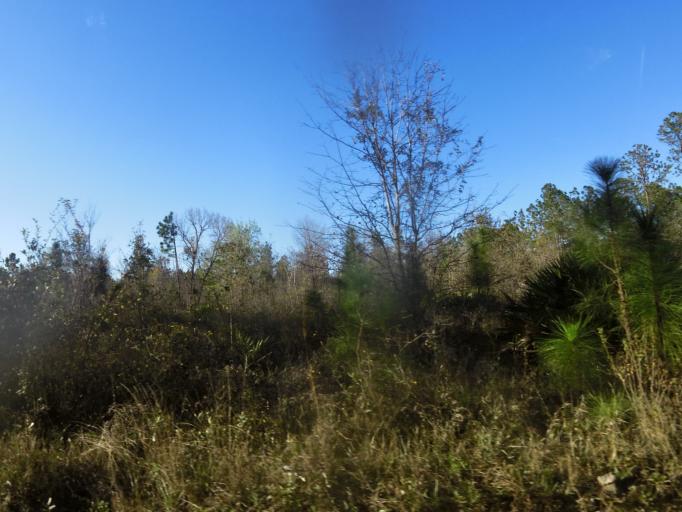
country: US
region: Florida
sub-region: Clay County
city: Middleburg
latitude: 30.1495
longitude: -81.8922
